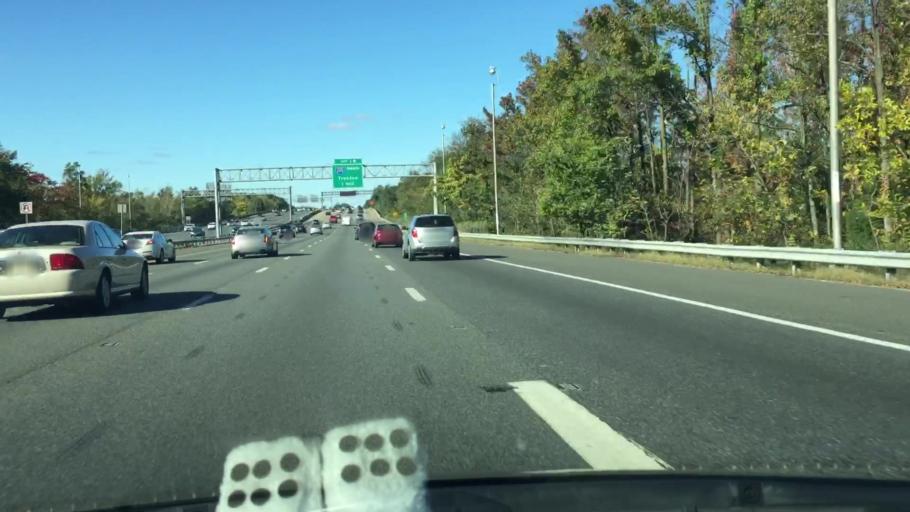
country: US
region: New Jersey
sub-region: Camden County
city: Bellmawr
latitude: 39.8503
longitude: -75.0962
